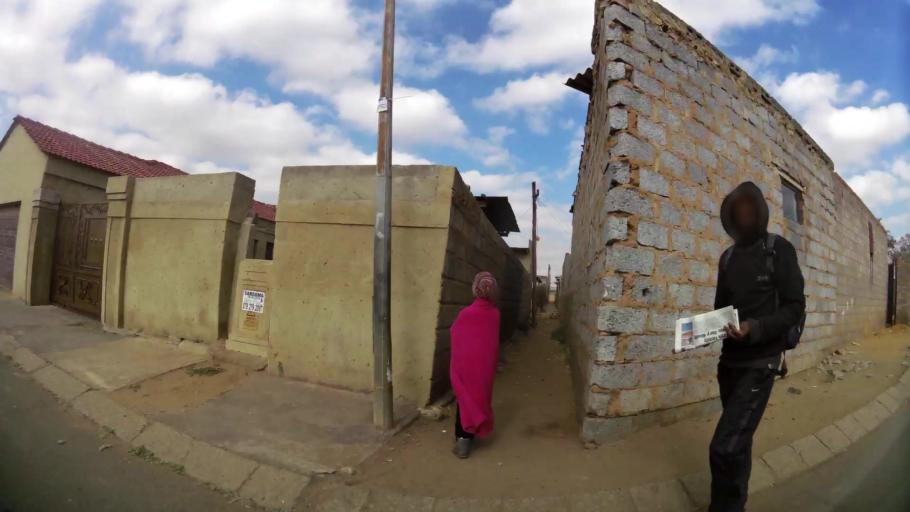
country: ZA
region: Gauteng
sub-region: City of Johannesburg Metropolitan Municipality
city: Roodepoort
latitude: -26.2147
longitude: 27.9056
